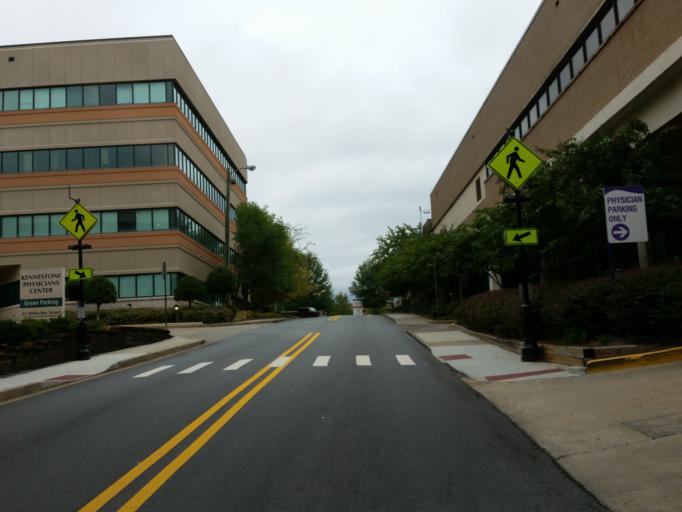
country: US
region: Georgia
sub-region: Cobb County
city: Marietta
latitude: 33.9675
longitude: -84.5510
